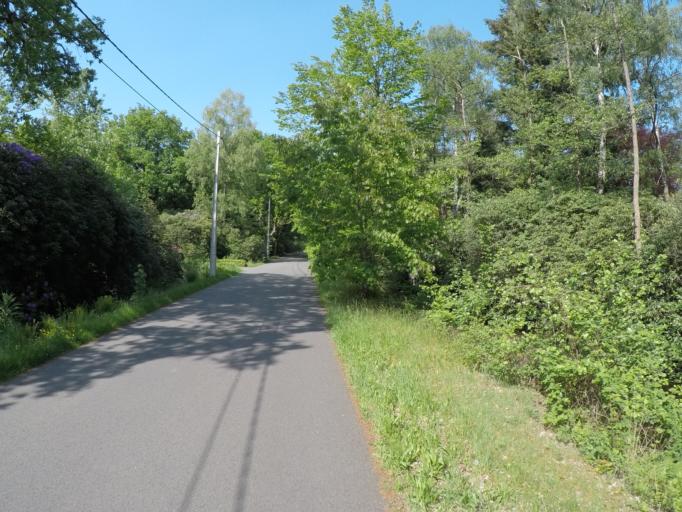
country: BE
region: Flanders
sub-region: Provincie Antwerpen
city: Schoten
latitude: 51.2626
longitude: 4.4838
